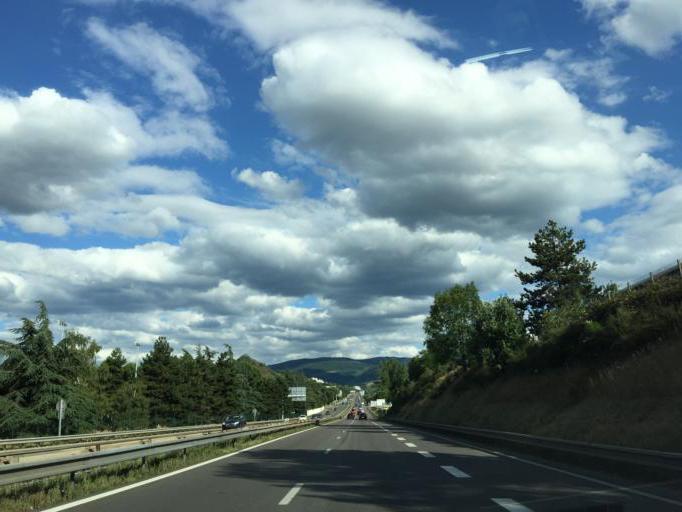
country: FR
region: Rhone-Alpes
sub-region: Departement de la Loire
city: Saint-Etienne
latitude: 45.4579
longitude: 4.4078
